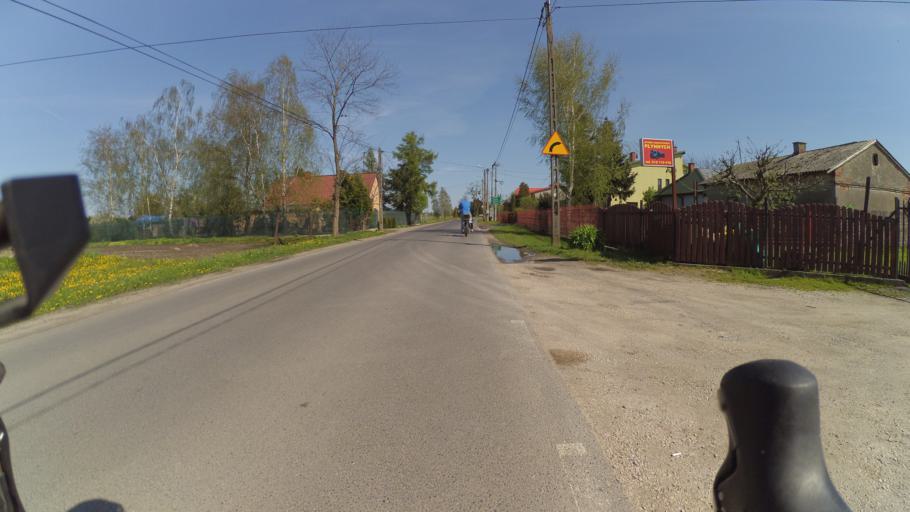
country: PL
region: Masovian Voivodeship
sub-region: Powiat warszawski zachodni
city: Leszno
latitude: 52.2443
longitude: 20.5473
